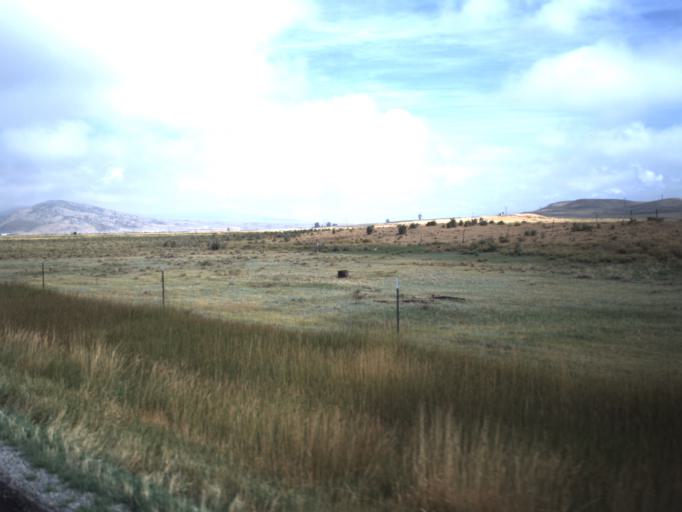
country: US
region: Utah
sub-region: Rich County
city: Randolph
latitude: 41.4921
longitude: -111.1197
